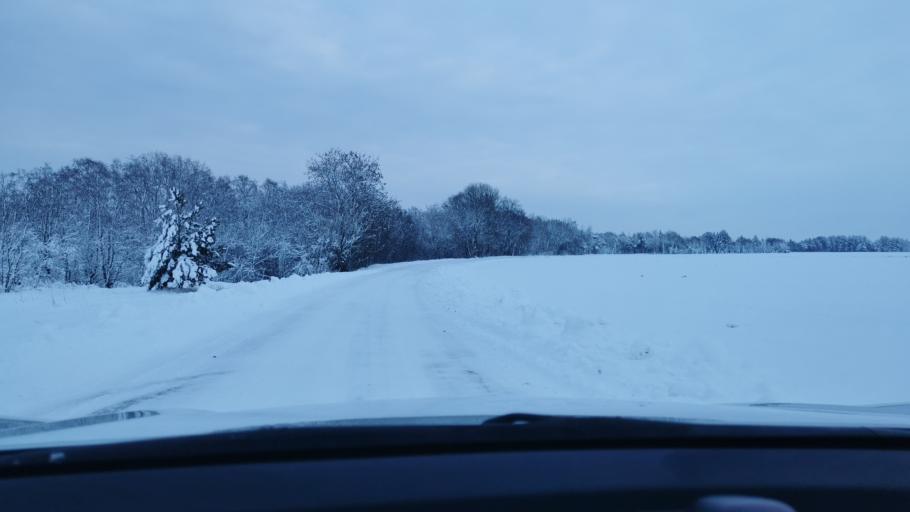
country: EE
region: Laeaene-Virumaa
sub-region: Haljala vald
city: Haljala
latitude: 59.5056
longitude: 26.2829
